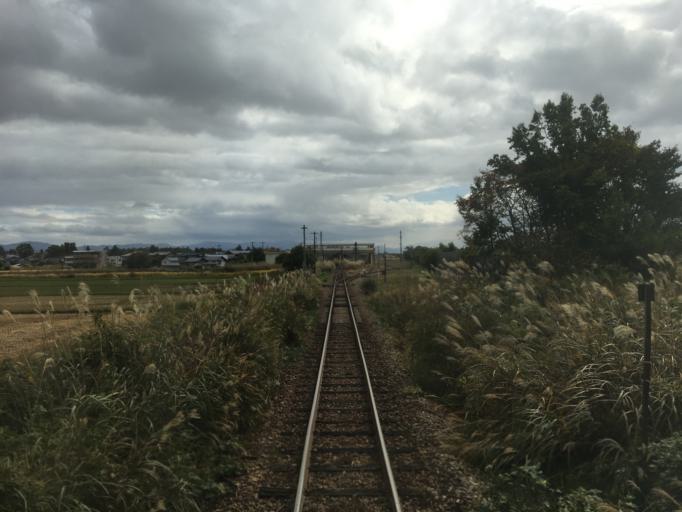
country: JP
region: Yamagata
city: Nagai
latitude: 38.0589
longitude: 140.0421
